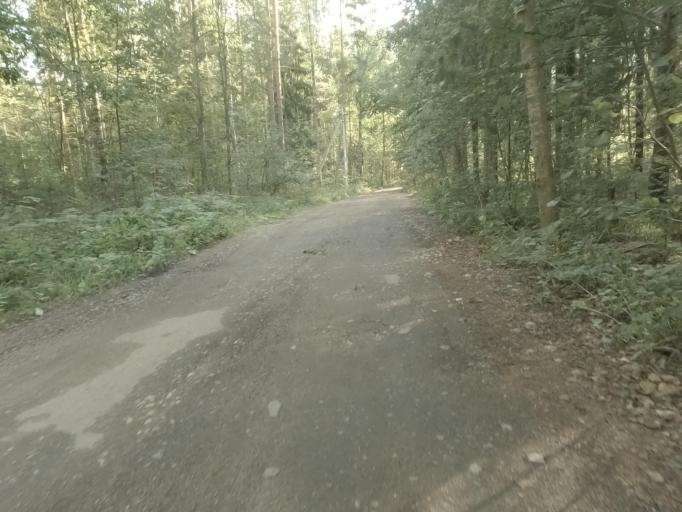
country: RU
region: Leningrad
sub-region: Volosovskiy Rayon
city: Shlissel'burg
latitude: 59.9459
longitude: 30.9867
